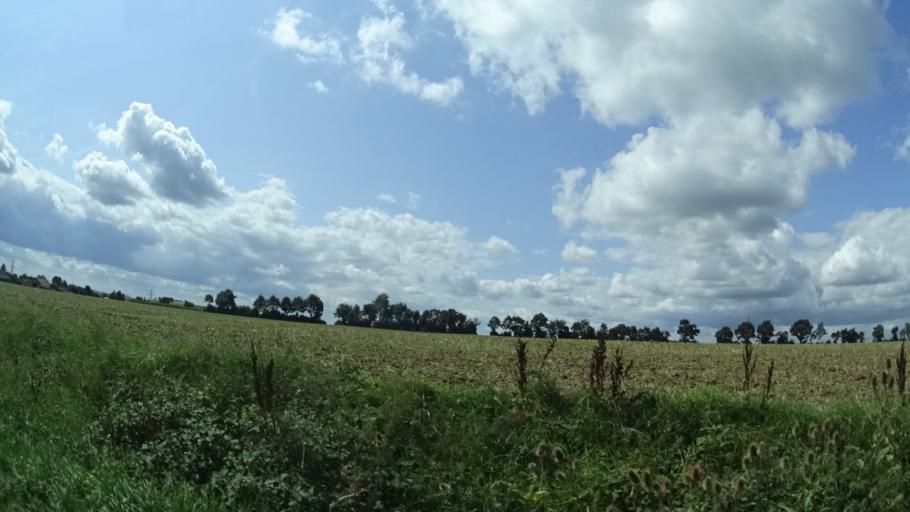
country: DE
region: Bavaria
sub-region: Upper Franconia
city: Rodental
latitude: 50.2585
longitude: 11.0850
